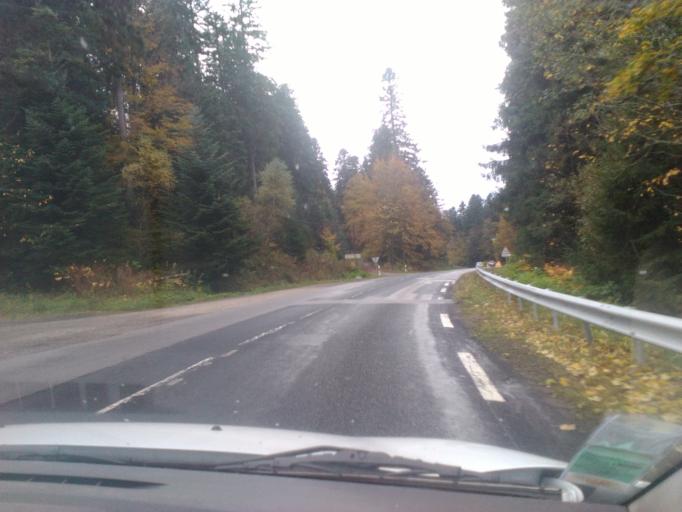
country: FR
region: Lorraine
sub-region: Departement des Vosges
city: Xonrupt-Longemer
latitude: 48.0984
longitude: 6.9050
